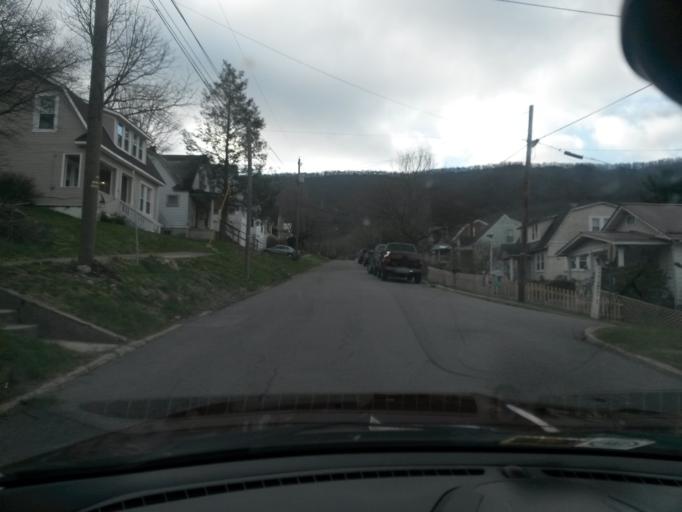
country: US
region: West Virginia
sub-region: Mercer County
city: Bluefield
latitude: 37.2521
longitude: -81.2157
